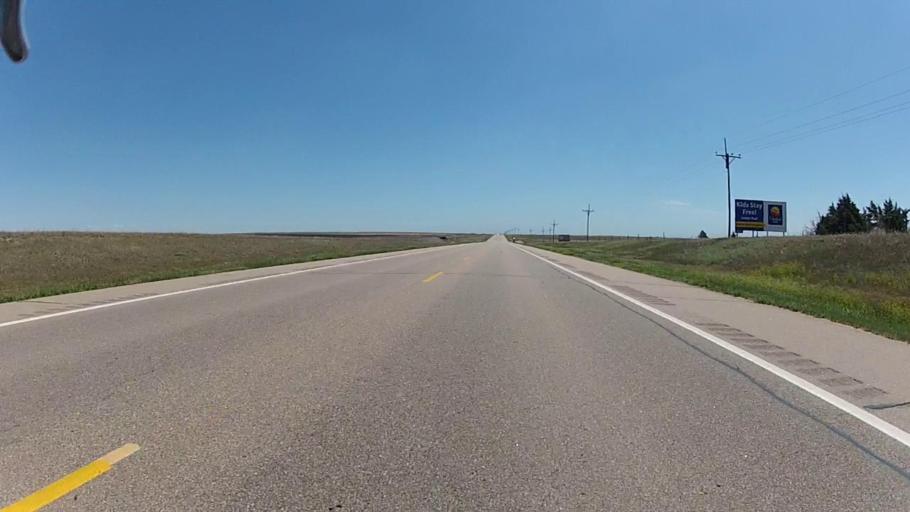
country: US
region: Kansas
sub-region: Ford County
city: Dodge City
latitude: 37.7092
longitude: -100.1220
